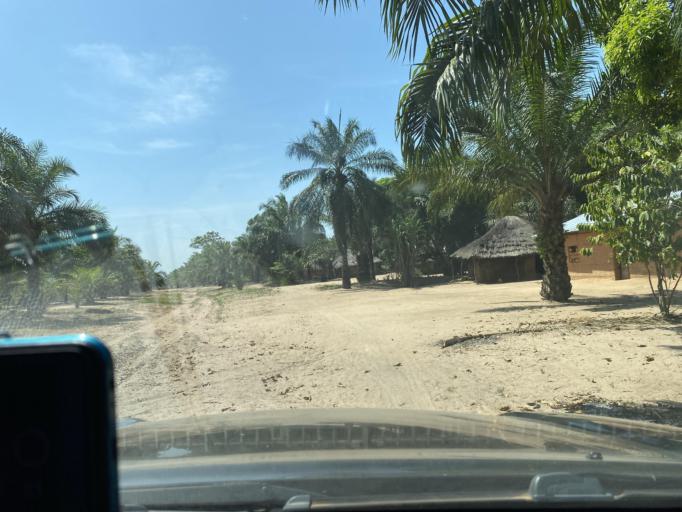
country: CD
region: Kasai-Oriental
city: Kabinda
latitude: -5.9166
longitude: 24.8497
